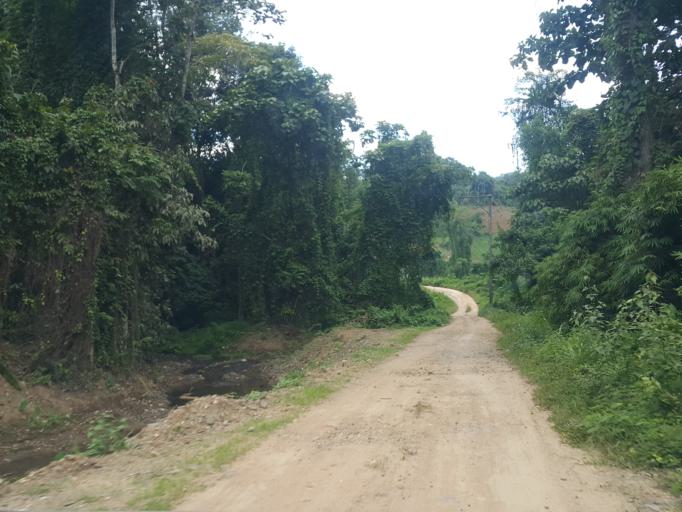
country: TH
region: Chiang Mai
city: Phrao
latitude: 19.3191
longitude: 99.1216
